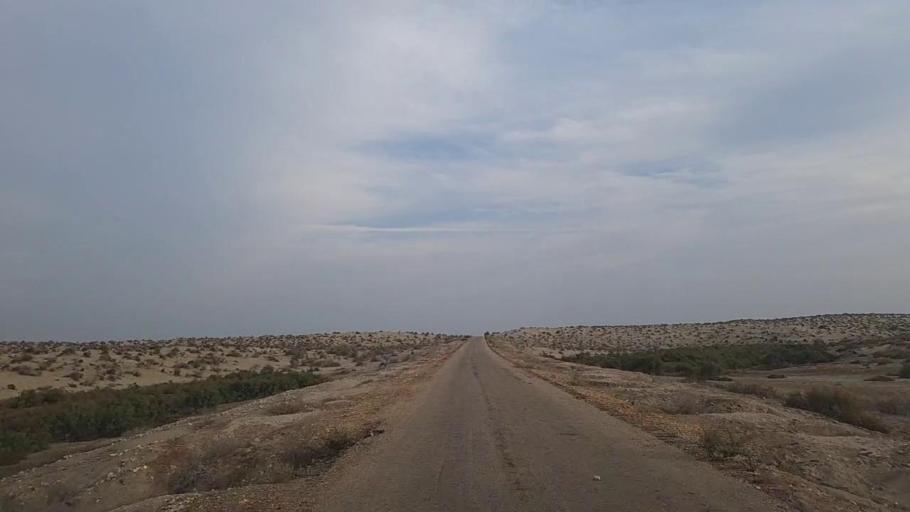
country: PK
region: Sindh
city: Daur
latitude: 26.5102
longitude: 68.5083
